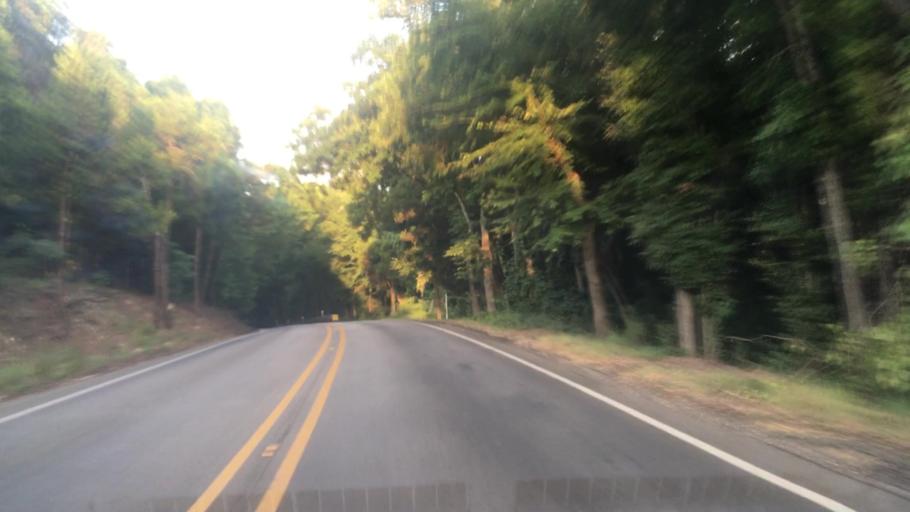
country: US
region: Texas
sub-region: Williamson County
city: Anderson Mill
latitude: 30.4497
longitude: -97.8557
